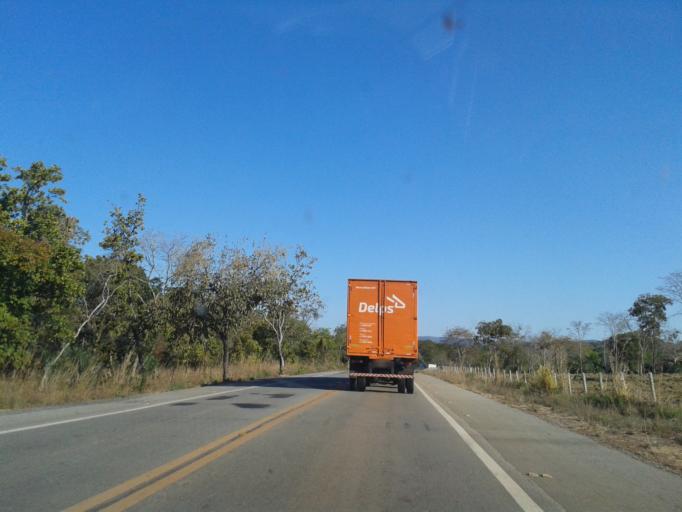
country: BR
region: Goias
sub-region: Itapirapua
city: Itapirapua
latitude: -15.3088
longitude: -50.4433
